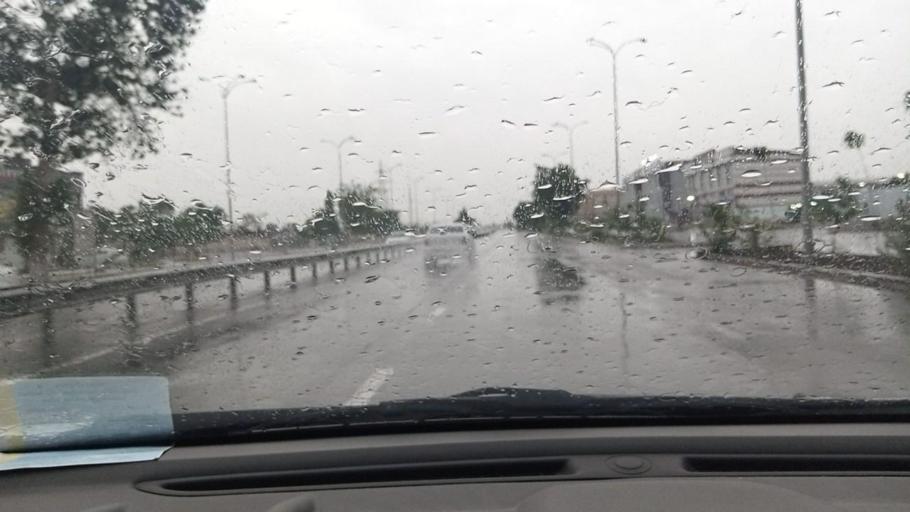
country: UZ
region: Toshkent
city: Ohangaron
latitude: 40.9011
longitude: 69.6515
